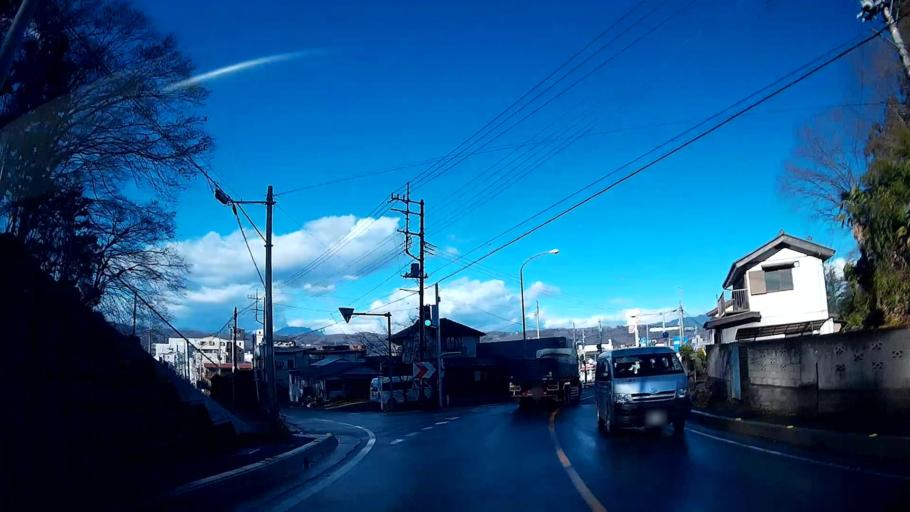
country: JP
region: Saitama
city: Chichibu
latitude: 35.9919
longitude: 139.0910
